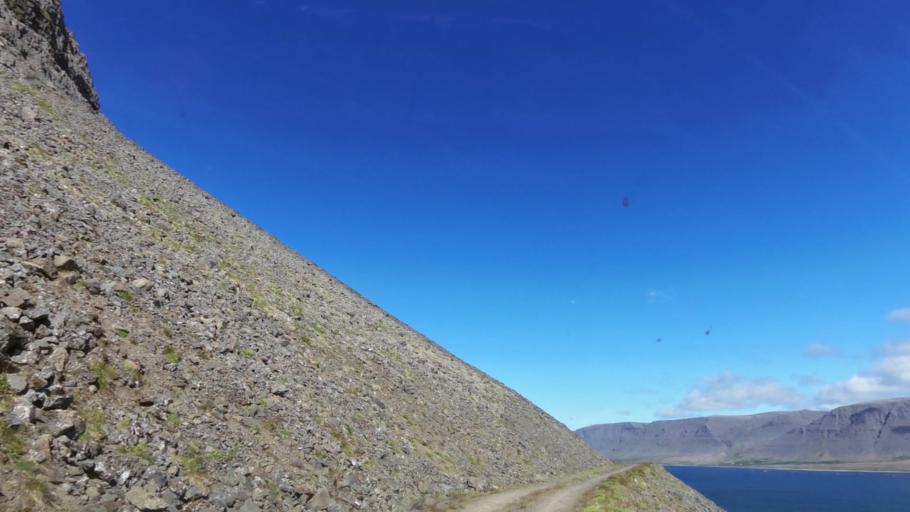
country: IS
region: West
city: Olafsvik
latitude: 65.6316
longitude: -23.9162
